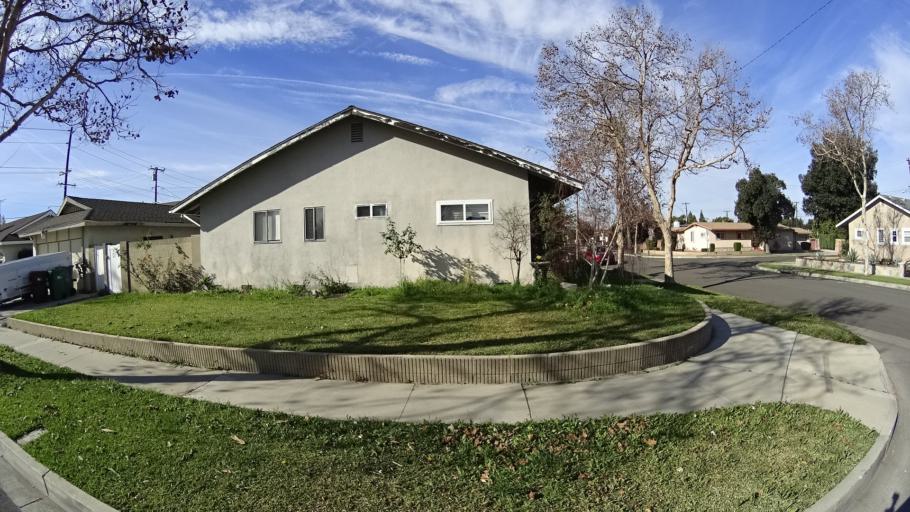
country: US
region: California
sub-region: Orange County
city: Fountain Valley
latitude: 33.7387
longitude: -117.9400
